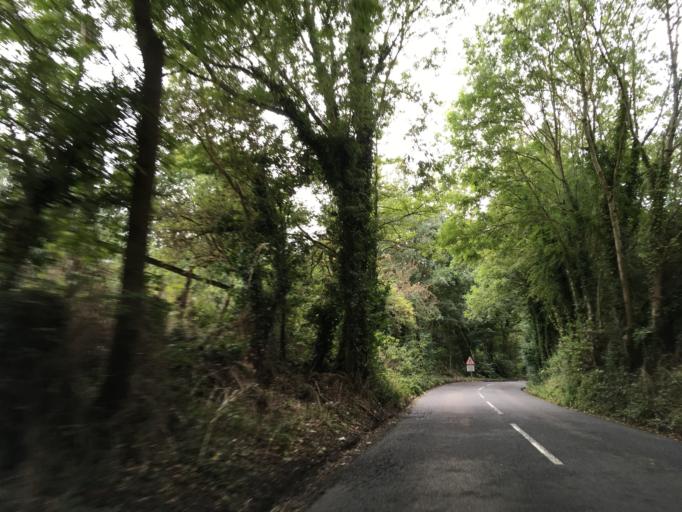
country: GB
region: England
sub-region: South Gloucestershire
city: Siston
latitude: 51.4734
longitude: -2.4522
